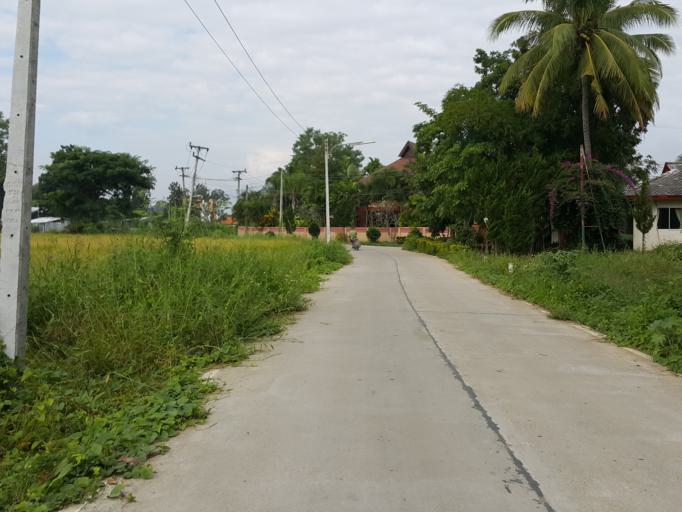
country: TH
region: Chiang Mai
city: San Kamphaeng
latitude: 18.7658
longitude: 99.1014
